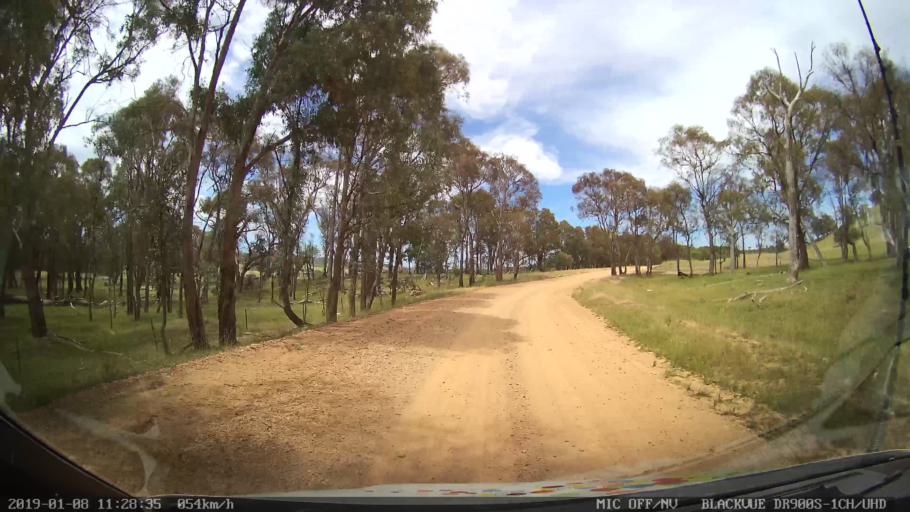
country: AU
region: New South Wales
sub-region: Guyra
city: Guyra
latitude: -30.2974
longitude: 151.5545
